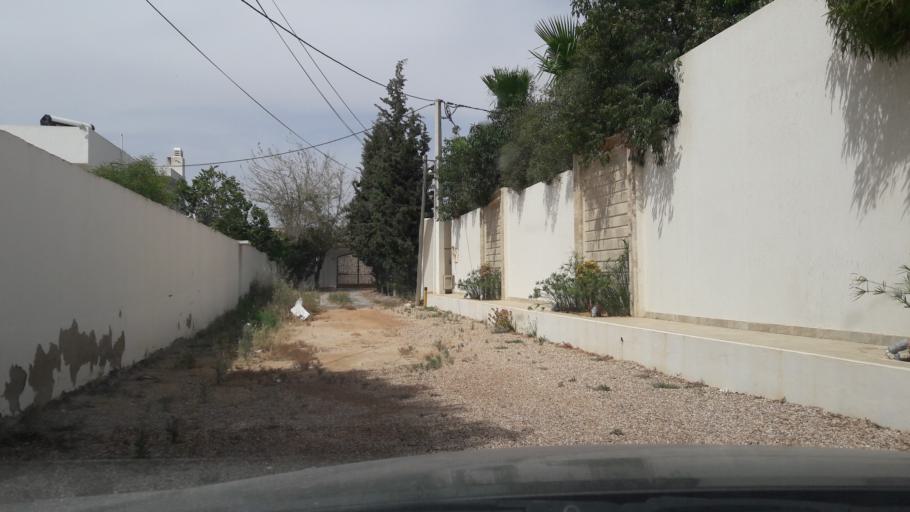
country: TN
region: Safaqis
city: Al Qarmadah
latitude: 34.7872
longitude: 10.7563
